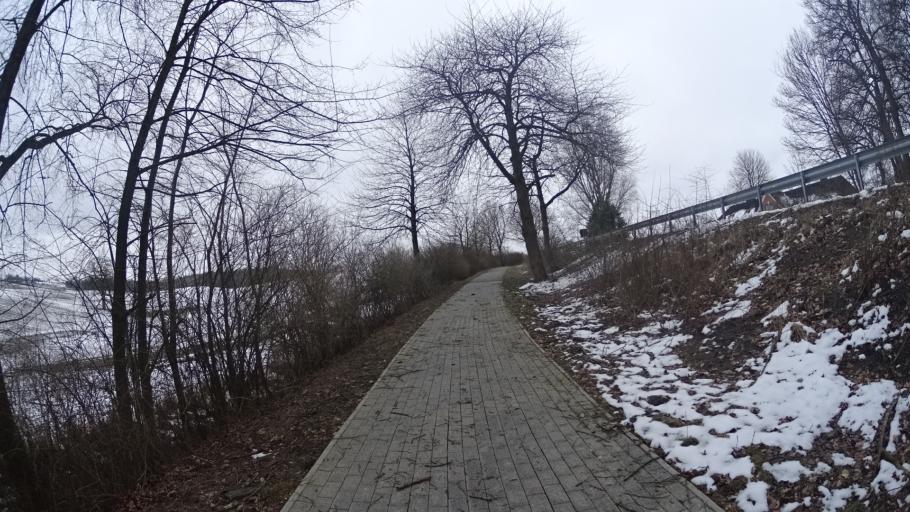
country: DE
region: Schleswig-Holstein
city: Panker
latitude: 54.3250
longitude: 10.5707
